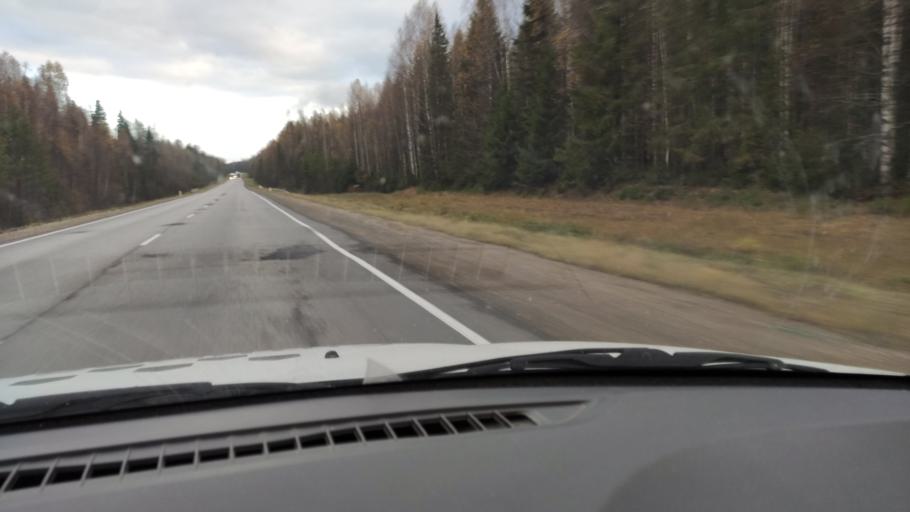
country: RU
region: Kirov
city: Chernaya Kholunitsa
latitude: 58.8411
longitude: 51.7503
